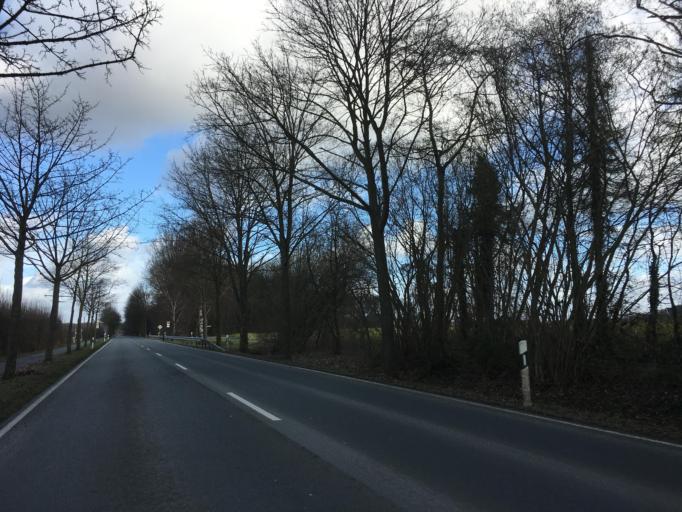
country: DE
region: North Rhine-Westphalia
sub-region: Regierungsbezirk Munster
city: Havixbeck
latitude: 51.9843
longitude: 7.4444
